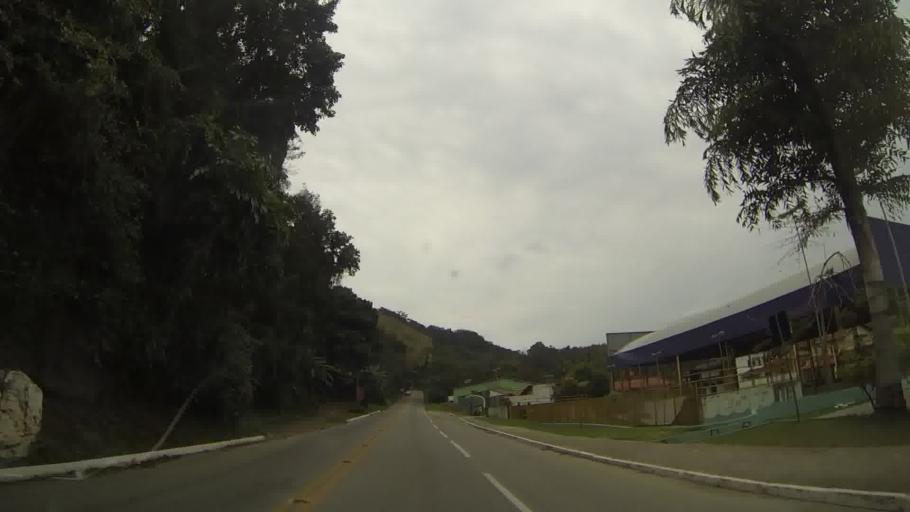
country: BR
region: Sao Paulo
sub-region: Sao Sebastiao
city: Sao Sebastiao
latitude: -23.8241
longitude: -45.4312
